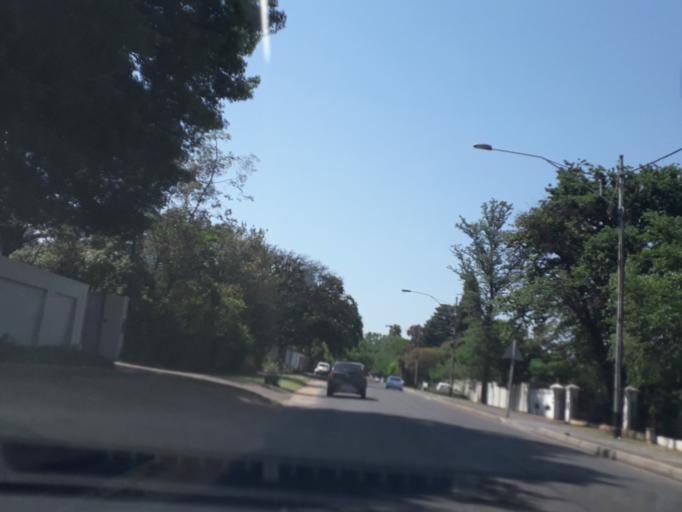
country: ZA
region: Gauteng
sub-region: City of Johannesburg Metropolitan Municipality
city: Johannesburg
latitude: -26.1296
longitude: 28.0238
